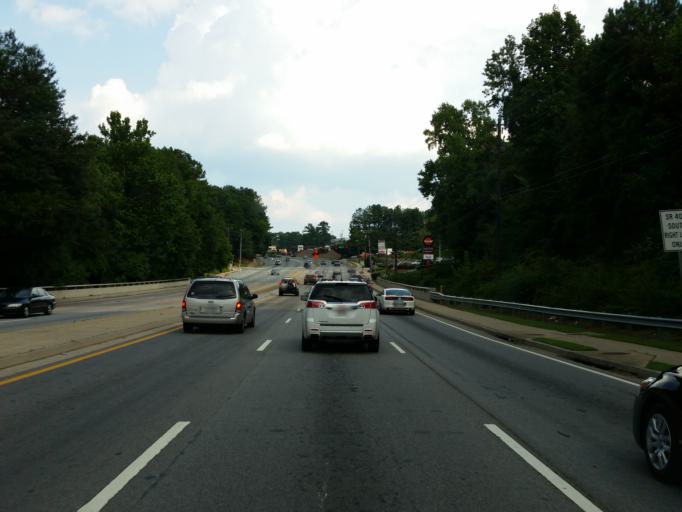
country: US
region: Georgia
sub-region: Fulton County
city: Roswell
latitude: 34.0250
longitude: -84.3313
